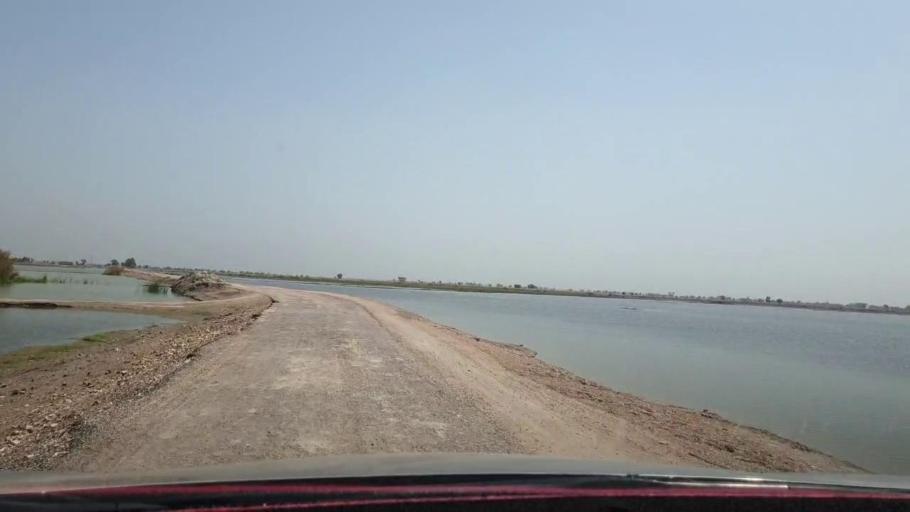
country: PK
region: Sindh
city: Warah
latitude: 27.3871
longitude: 67.7802
